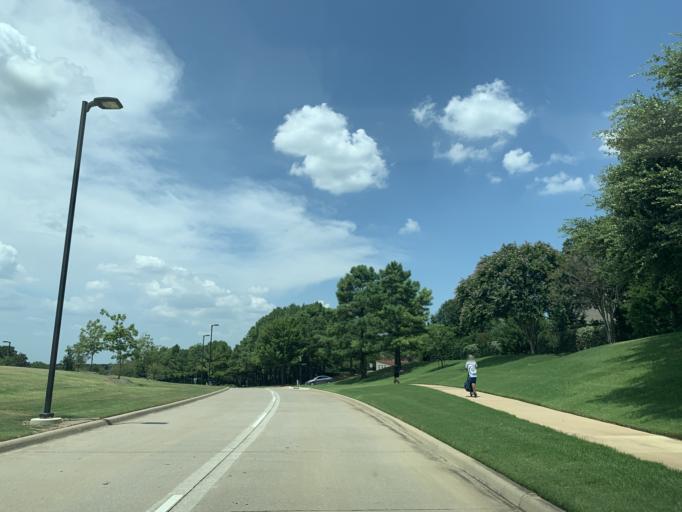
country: US
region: Texas
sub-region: Tarrant County
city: Southlake
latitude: 32.9726
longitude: -97.1545
